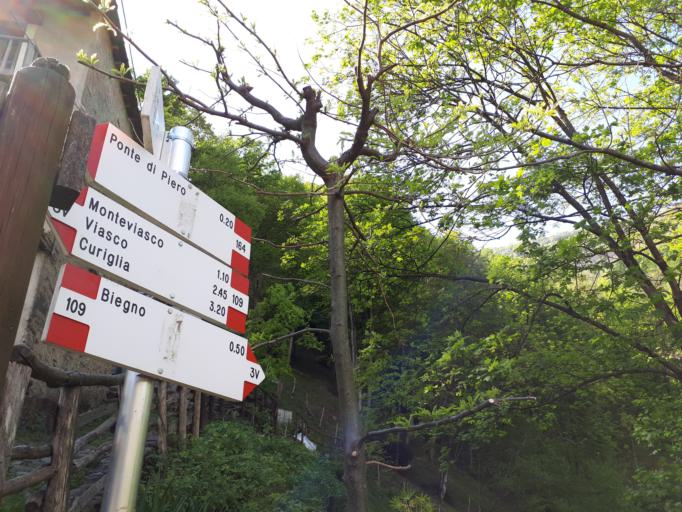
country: IT
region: Lombardy
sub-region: Provincia di Varese
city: Veddasca
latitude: 46.0762
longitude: 8.8166
